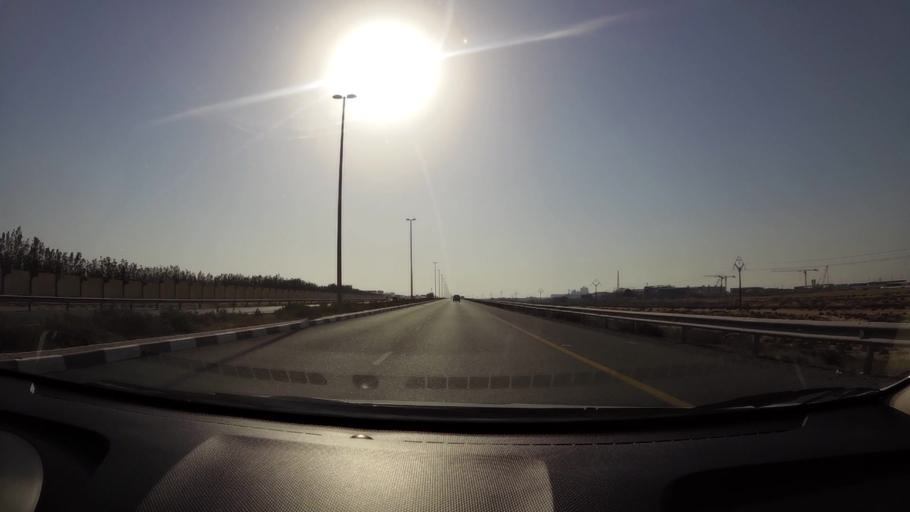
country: AE
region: Umm al Qaywayn
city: Umm al Qaywayn
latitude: 25.4335
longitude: 55.5725
